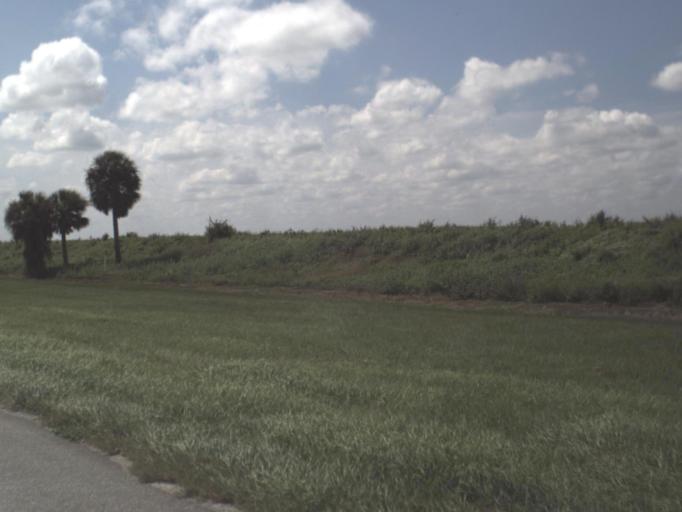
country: US
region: Florida
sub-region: Hendry County
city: Port LaBelle
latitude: 26.6106
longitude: -81.4366
